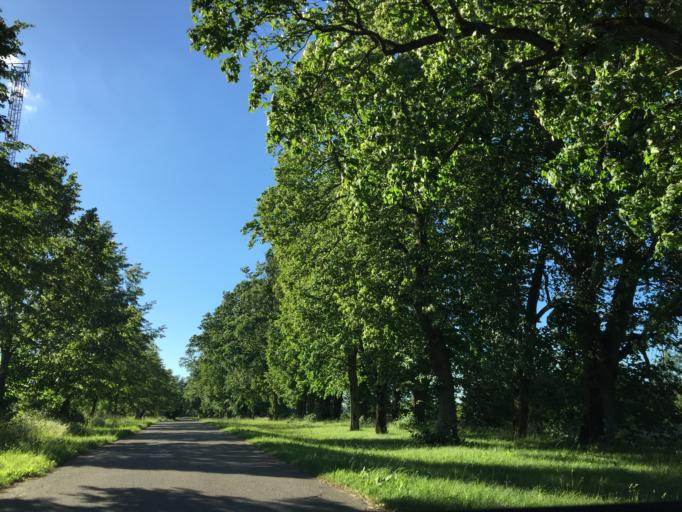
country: LV
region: Ventspils Rajons
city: Piltene
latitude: 57.4036
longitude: 21.8540
